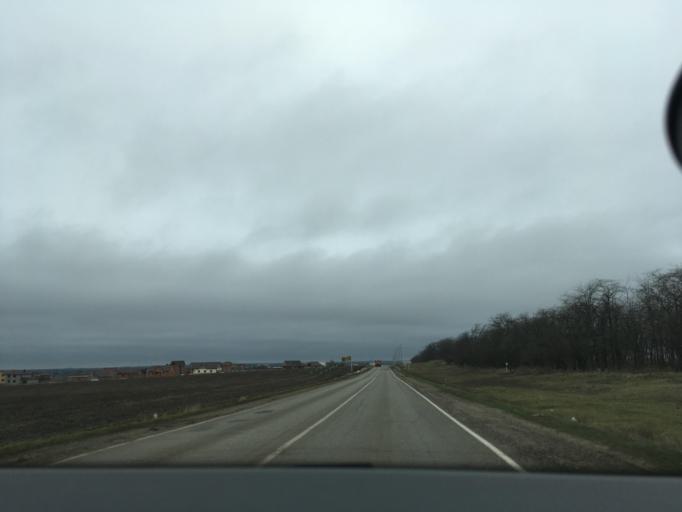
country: RU
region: Krasnodarskiy
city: Kushchevskaya
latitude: 46.5888
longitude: 39.6437
